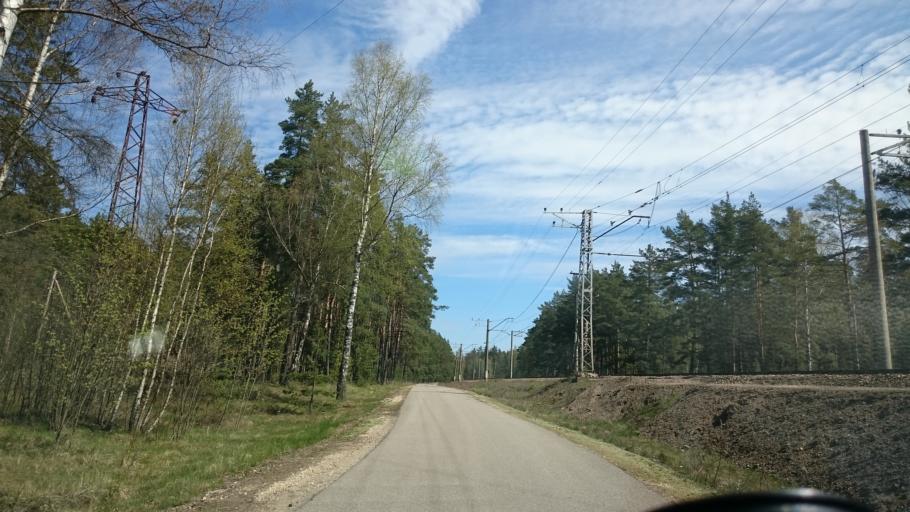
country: LV
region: Saulkrastu
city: Saulkrasti
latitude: 57.1918
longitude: 24.3510
